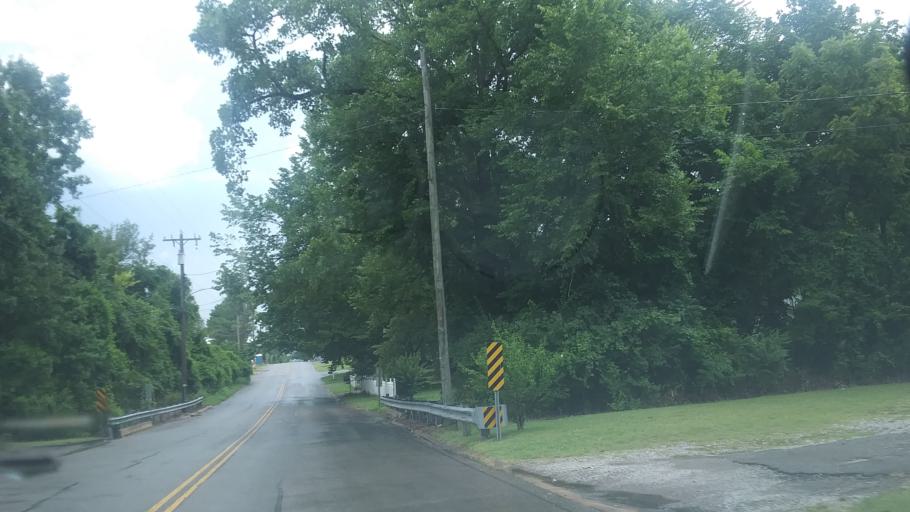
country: US
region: Tennessee
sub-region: Davidson County
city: Belle Meade
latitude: 36.1560
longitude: -86.8847
